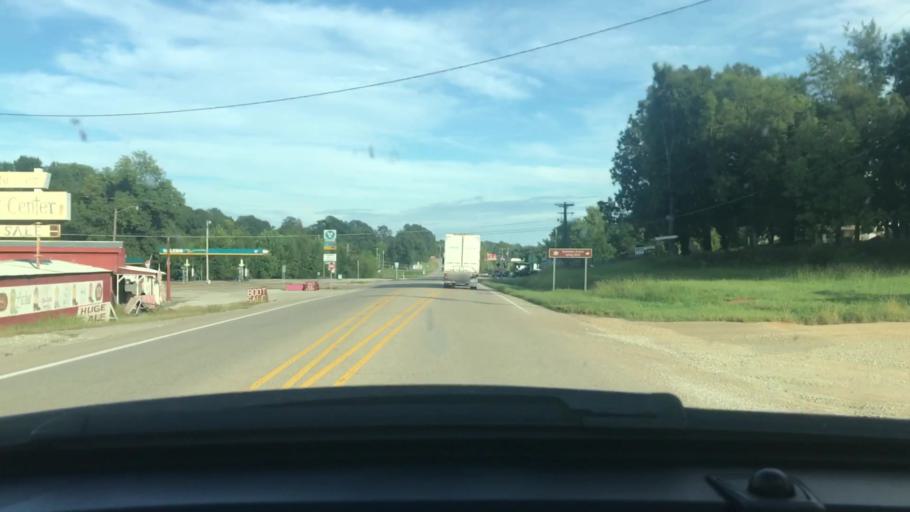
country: US
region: Arkansas
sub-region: Sharp County
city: Cherokee Village
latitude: 36.2371
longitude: -91.2540
